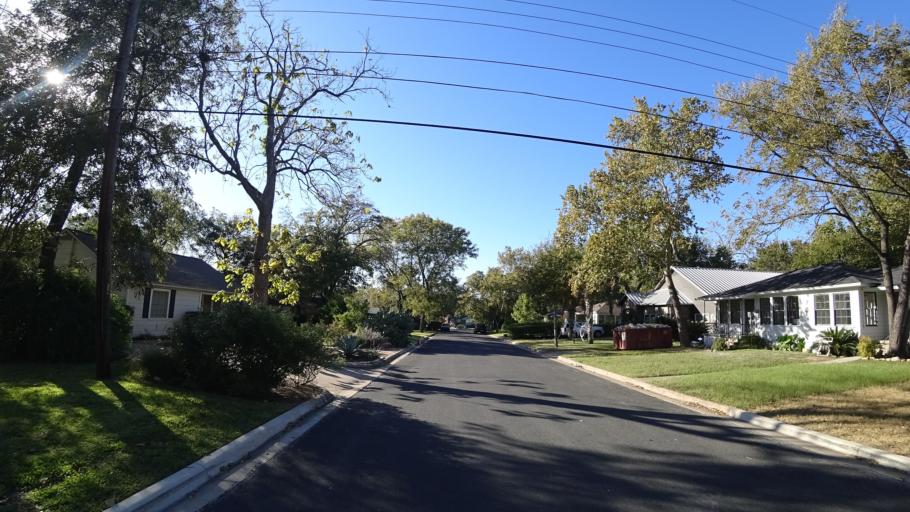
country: US
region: Texas
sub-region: Travis County
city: Austin
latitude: 30.3065
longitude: -97.7558
